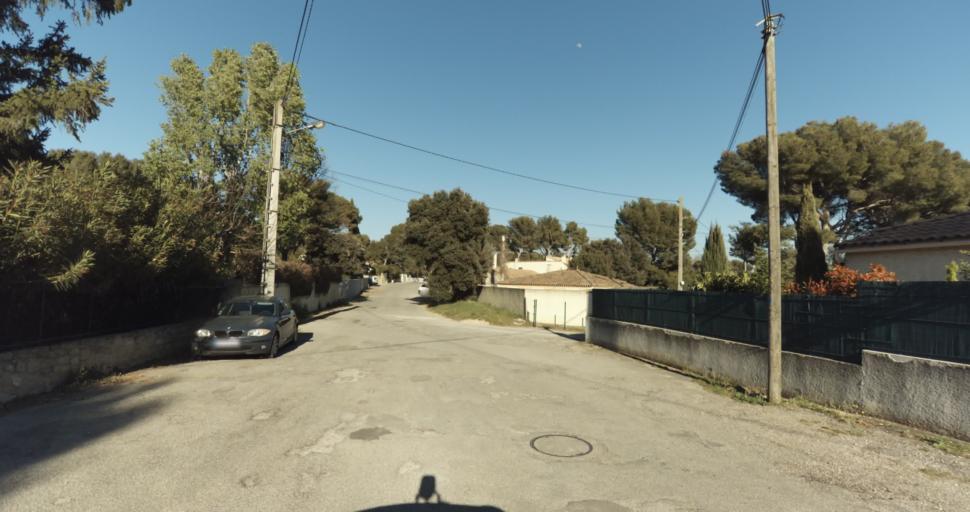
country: FR
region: Provence-Alpes-Cote d'Azur
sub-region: Departement des Bouches-du-Rhone
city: Pelissanne
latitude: 43.6386
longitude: 5.1487
